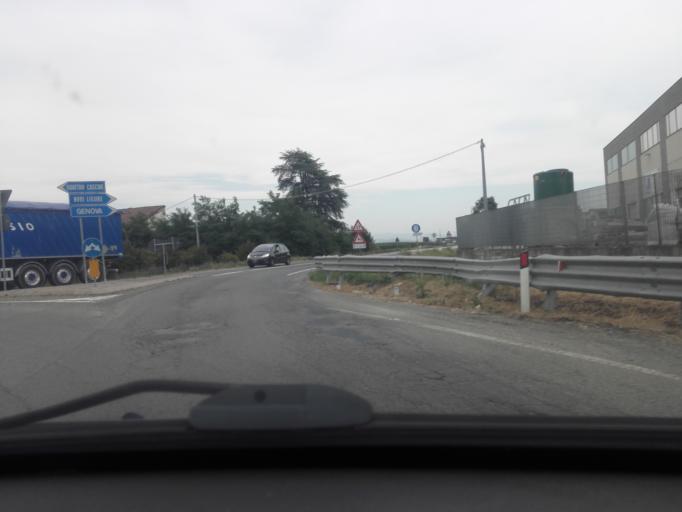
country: IT
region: Piedmont
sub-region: Provincia di Alessandria
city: Mandrogne
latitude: 44.8378
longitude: 8.7332
